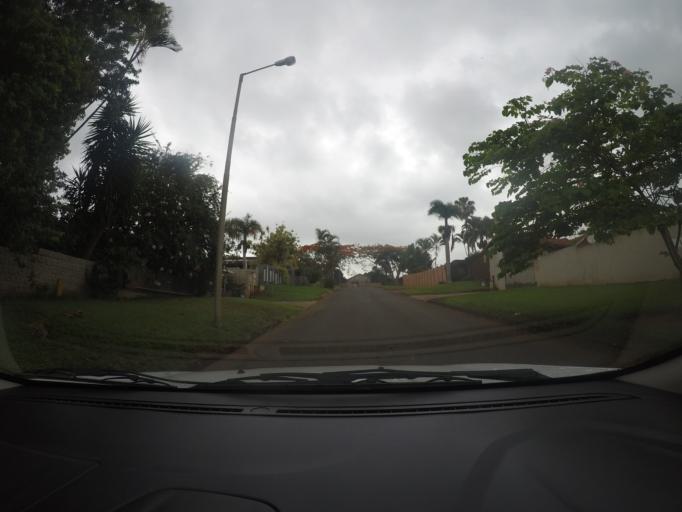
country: ZA
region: KwaZulu-Natal
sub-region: uThungulu District Municipality
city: Empangeni
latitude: -28.7644
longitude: 31.8998
